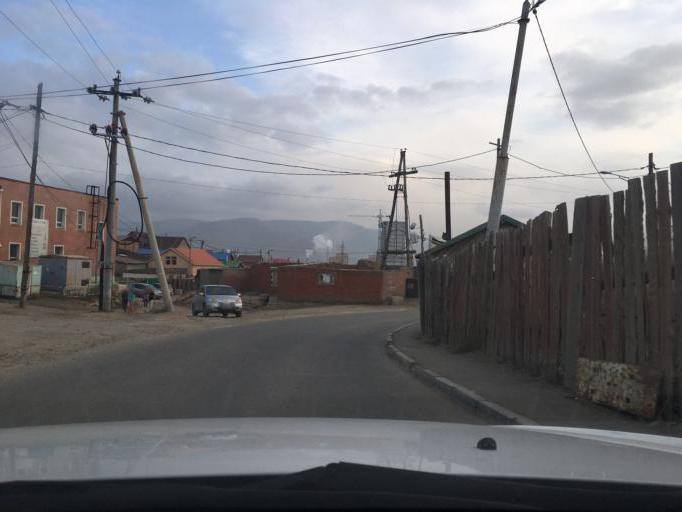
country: MN
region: Ulaanbaatar
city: Ulaanbaatar
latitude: 47.9263
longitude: 106.8574
